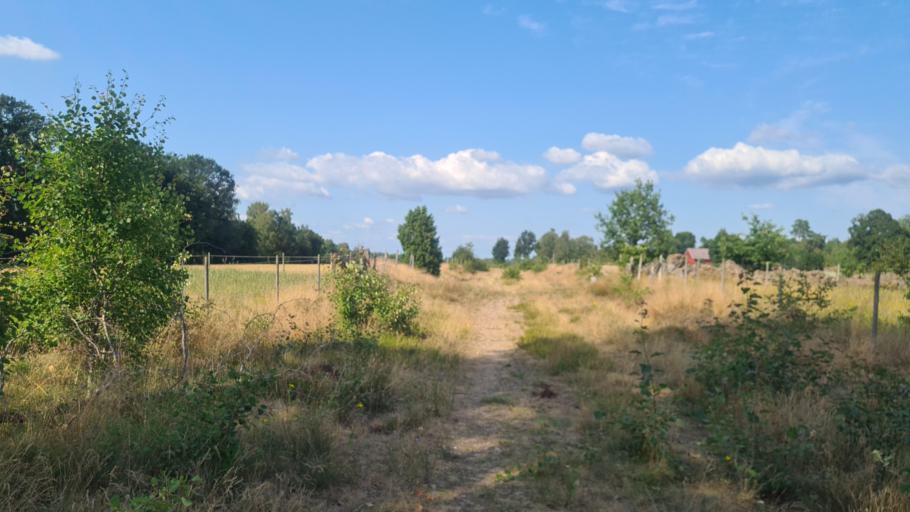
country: SE
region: Kronoberg
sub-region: Ljungby Kommun
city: Ljungby
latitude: 56.7453
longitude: 13.8790
